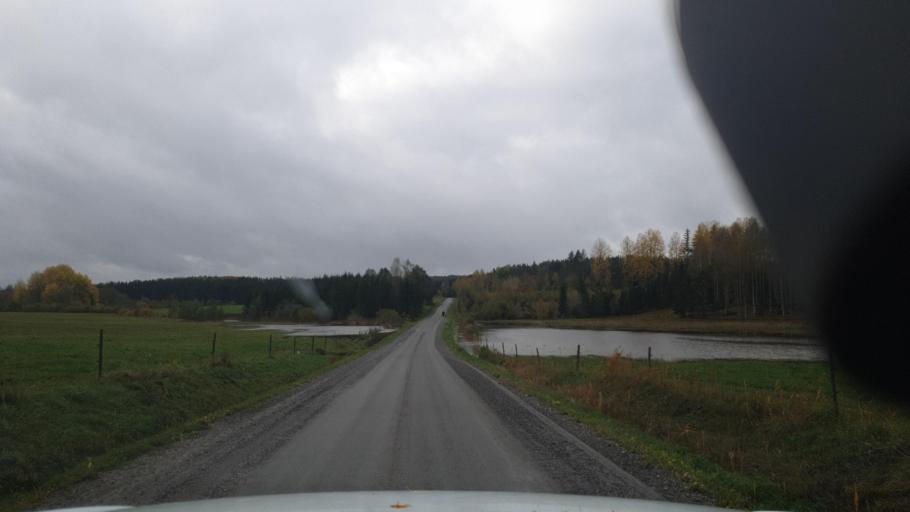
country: SE
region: Vaermland
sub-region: Karlstads Kommun
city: Edsvalla
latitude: 59.5531
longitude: 13.0109
